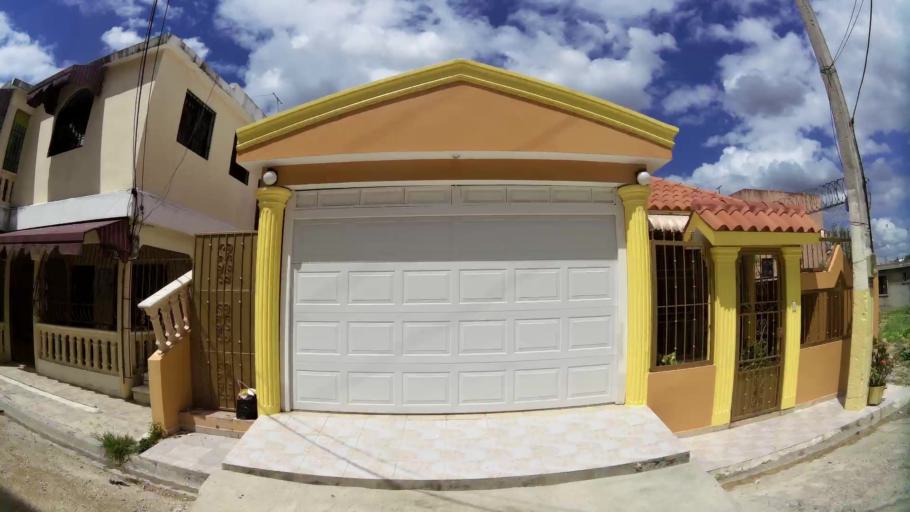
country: DO
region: Nacional
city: Ensanche Luperon
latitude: 18.5253
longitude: -69.8948
